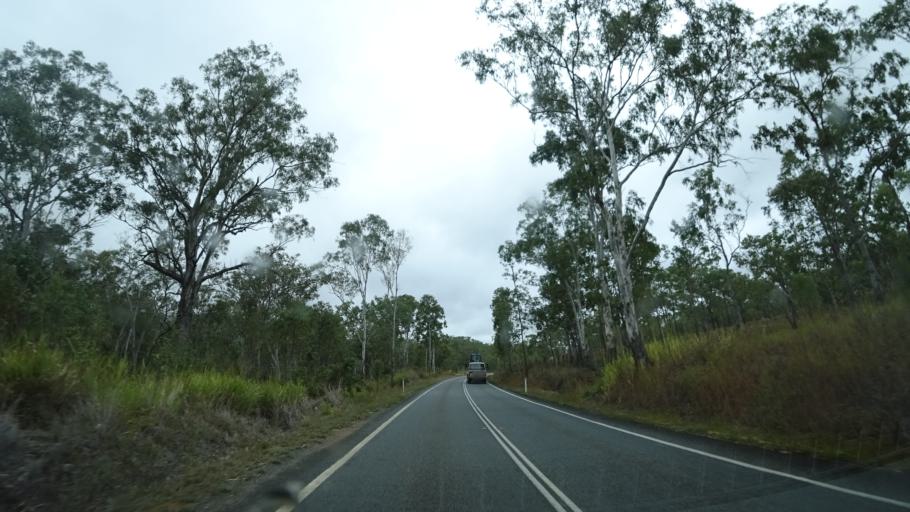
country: AU
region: Queensland
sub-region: Cairns
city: Port Douglas
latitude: -16.6971
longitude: 145.3457
